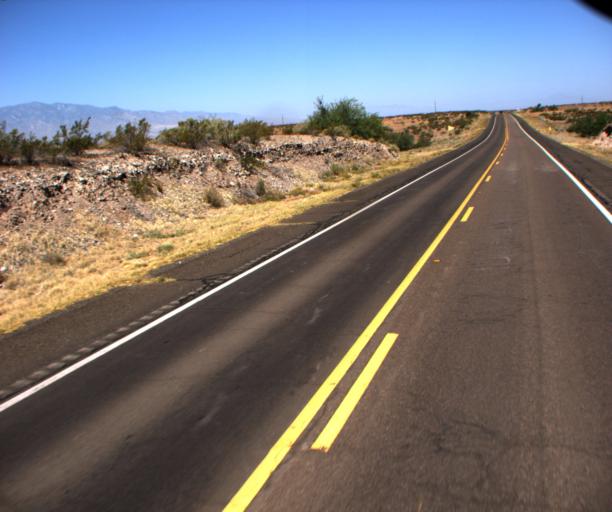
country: US
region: Arizona
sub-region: Graham County
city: Safford
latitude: 32.8004
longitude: -109.5683
